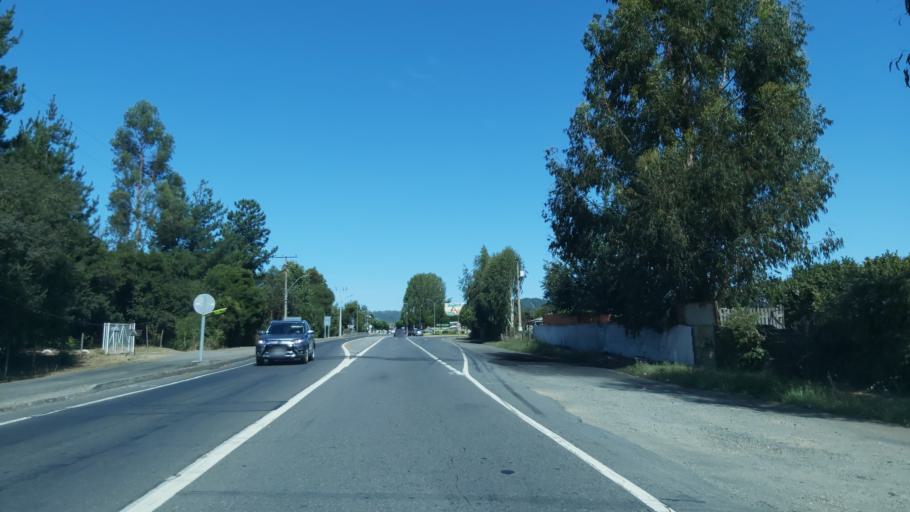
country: CL
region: Biobio
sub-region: Provincia de Concepcion
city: Lota
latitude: -37.1630
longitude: -72.9581
